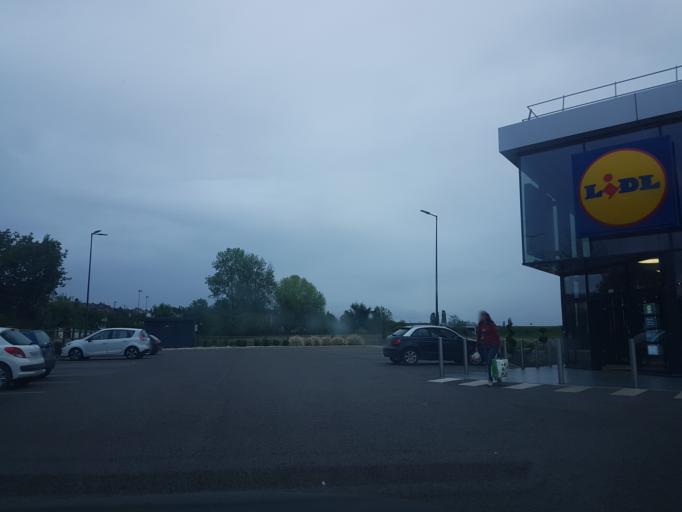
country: FR
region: Franche-Comte
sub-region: Departement de la Haute-Saone
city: Saint-Sauveur
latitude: 47.8156
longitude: 6.3911
